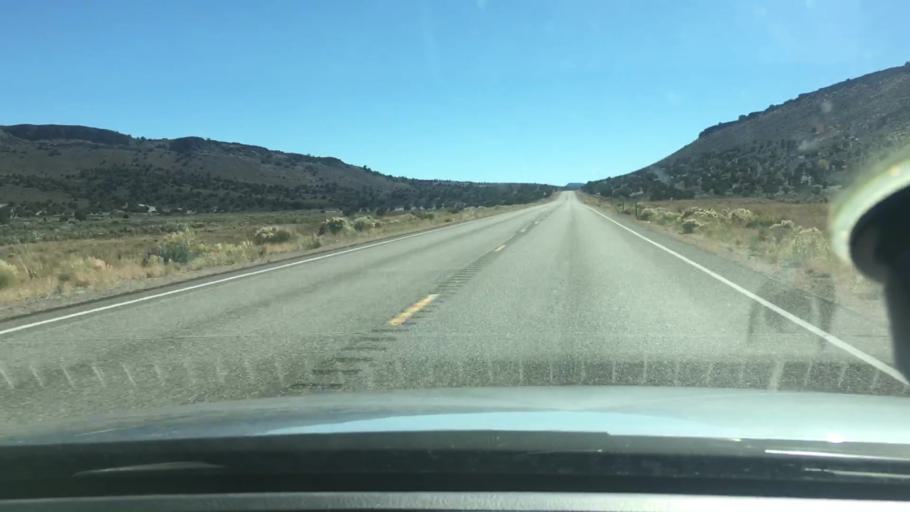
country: US
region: Nevada
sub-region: White Pine County
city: Ely
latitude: 38.9248
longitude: -115.1756
